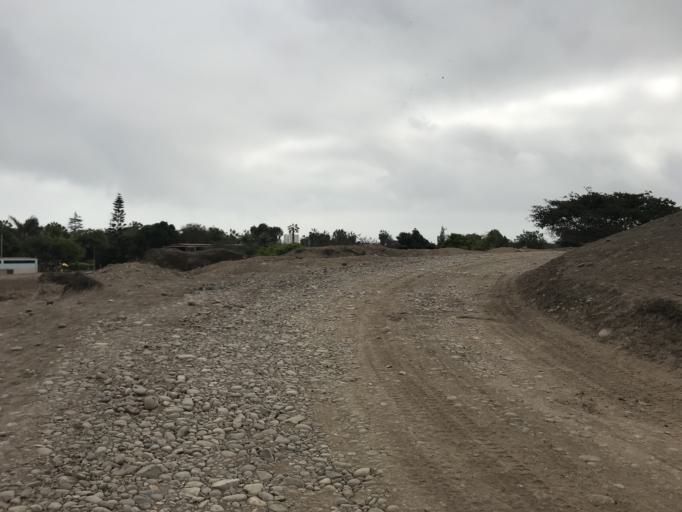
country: PE
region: Callao
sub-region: Callao
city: Callao
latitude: -12.0664
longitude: -77.0836
